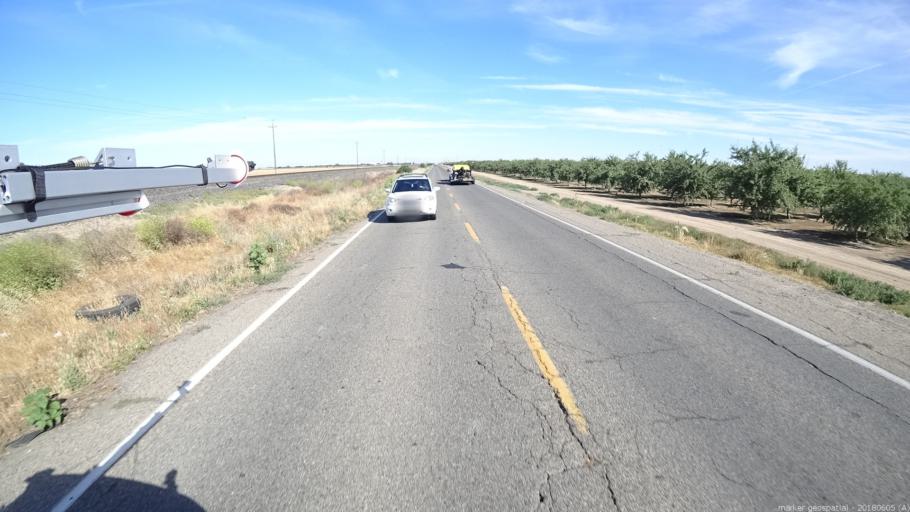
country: US
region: California
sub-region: Madera County
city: Chowchilla
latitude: 37.1280
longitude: -120.2609
